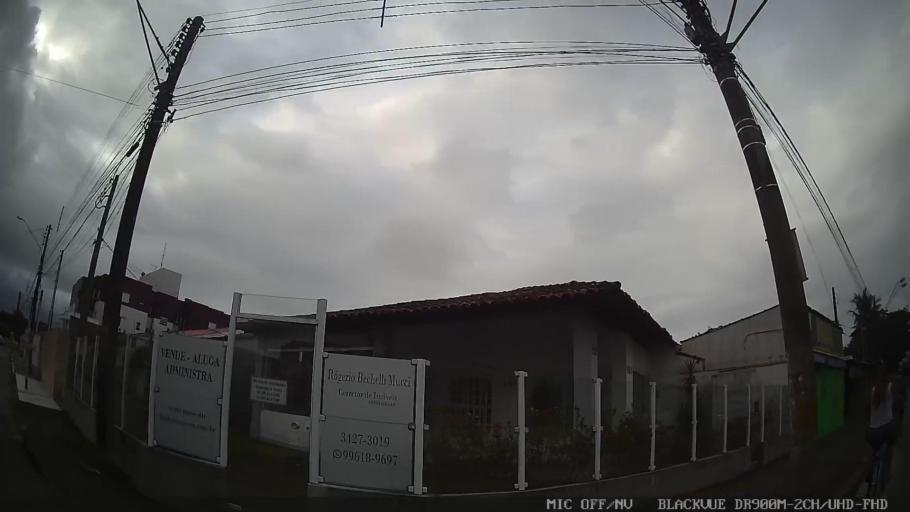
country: BR
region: Sao Paulo
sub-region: Itanhaem
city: Itanhaem
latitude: -24.1786
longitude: -46.7790
